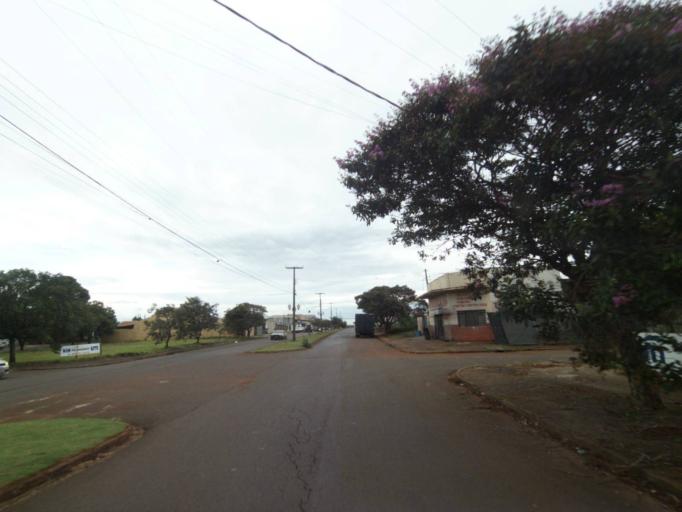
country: BR
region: Parana
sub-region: Campo Mourao
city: Campo Mourao
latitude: -24.0260
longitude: -52.3568
